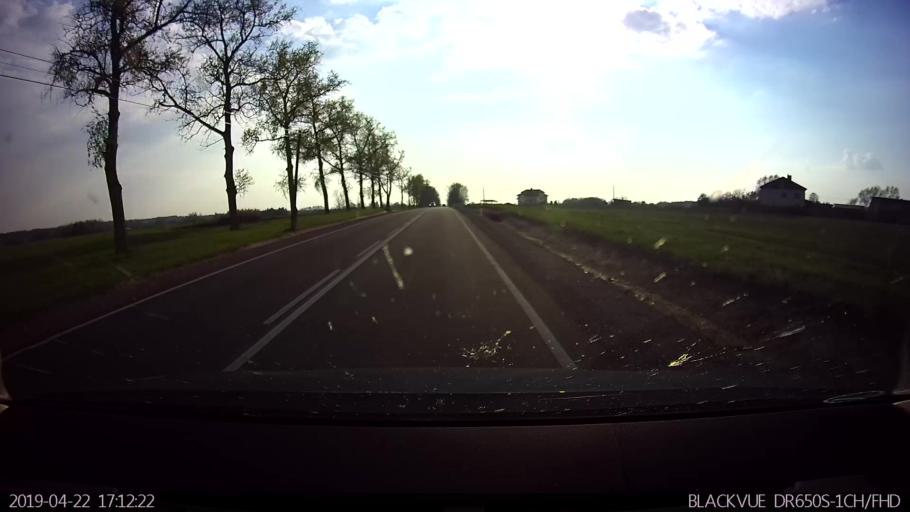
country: PL
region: Masovian Voivodeship
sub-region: Powiat siedlecki
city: Korczew
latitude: 52.4078
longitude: 22.5344
